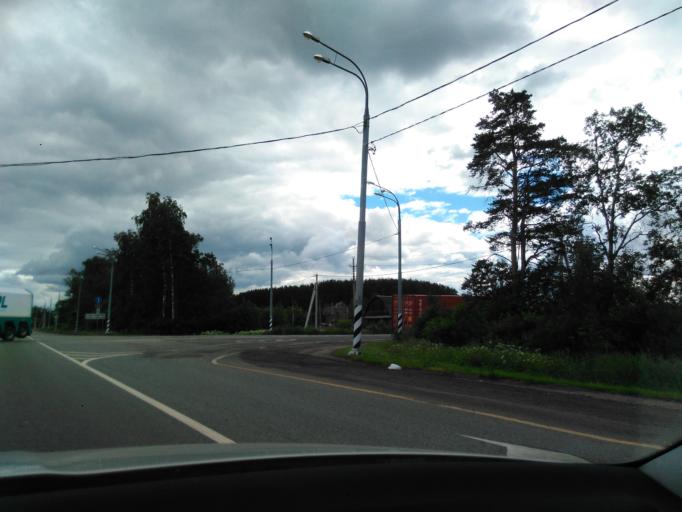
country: RU
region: Moskovskaya
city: Spas-Zaulok
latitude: 56.4903
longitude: 36.5615
